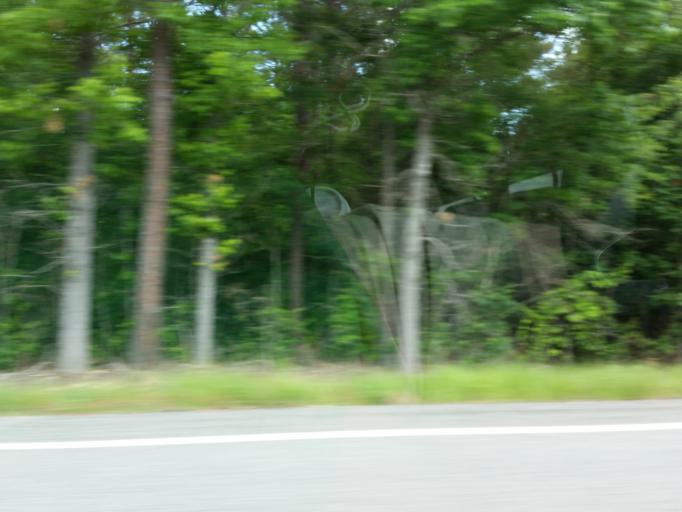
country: US
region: Alabama
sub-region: Sumter County
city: York
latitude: 32.3663
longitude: -88.1912
